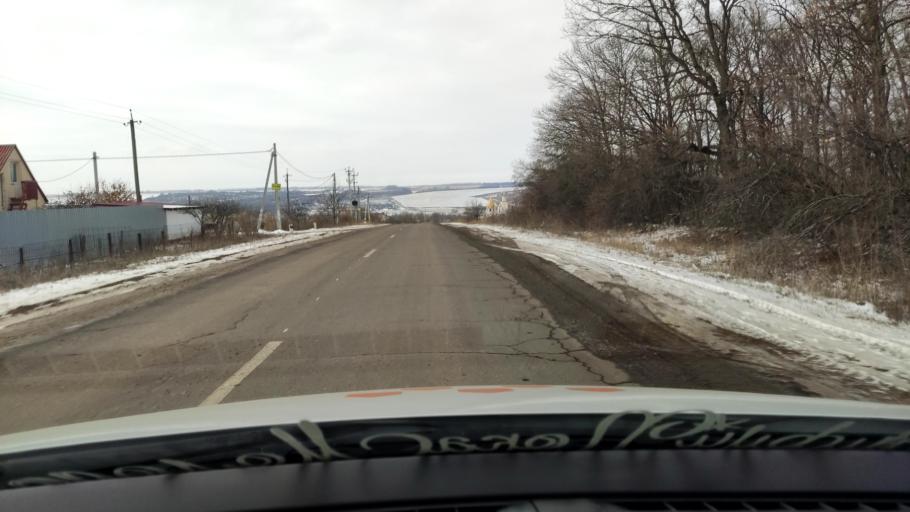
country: RU
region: Voronezj
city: Semiluki
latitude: 51.7490
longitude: 39.0396
